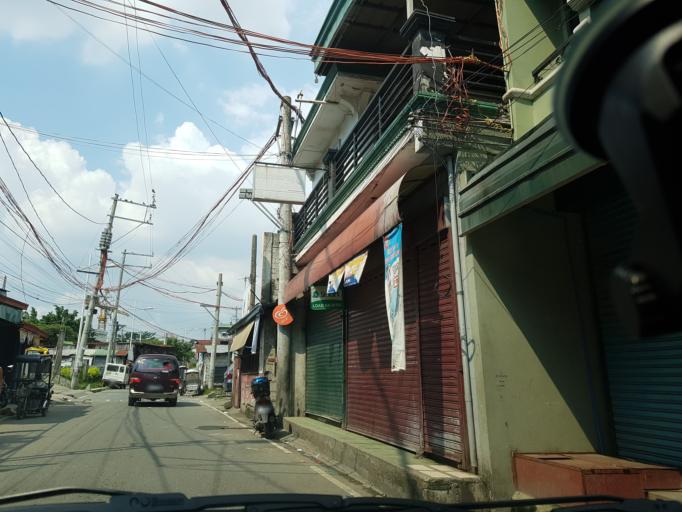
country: PH
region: Calabarzon
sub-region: Province of Rizal
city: Pateros
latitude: 14.5424
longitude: 121.0851
